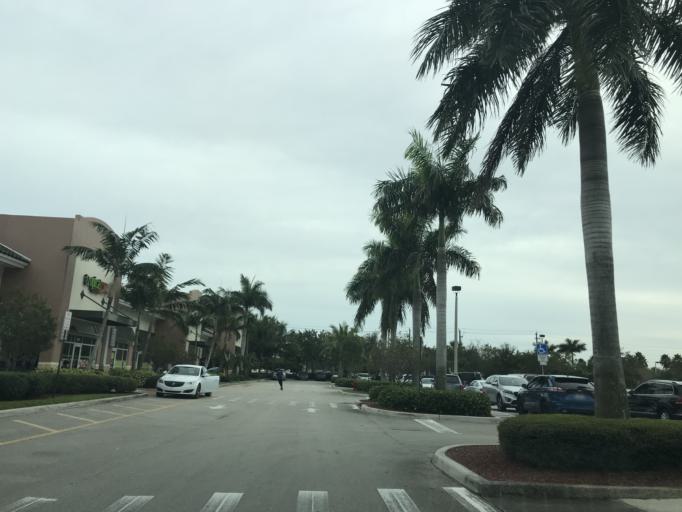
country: US
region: Florida
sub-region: Broward County
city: Margate
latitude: 26.2729
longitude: -80.2048
